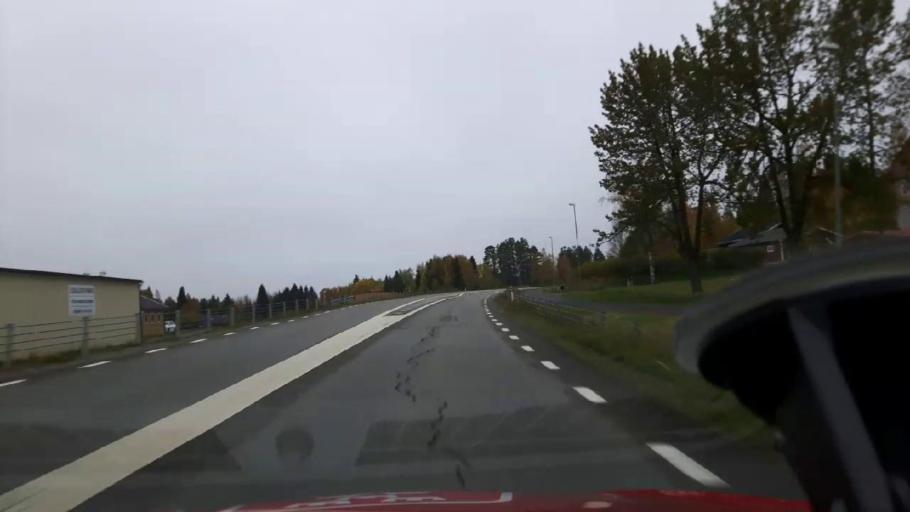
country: SE
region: Jaemtland
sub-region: Bergs Kommun
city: Hoverberg
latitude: 62.6929
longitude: 14.4043
